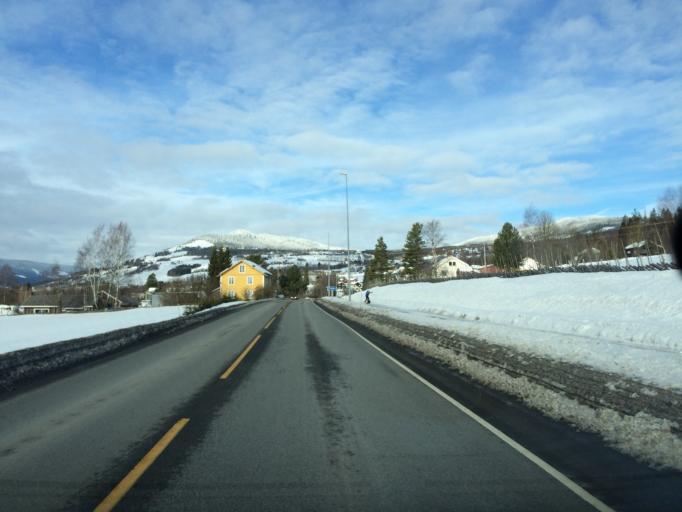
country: NO
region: Oppland
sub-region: Gausdal
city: Segalstad bru
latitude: 61.2100
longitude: 10.2968
